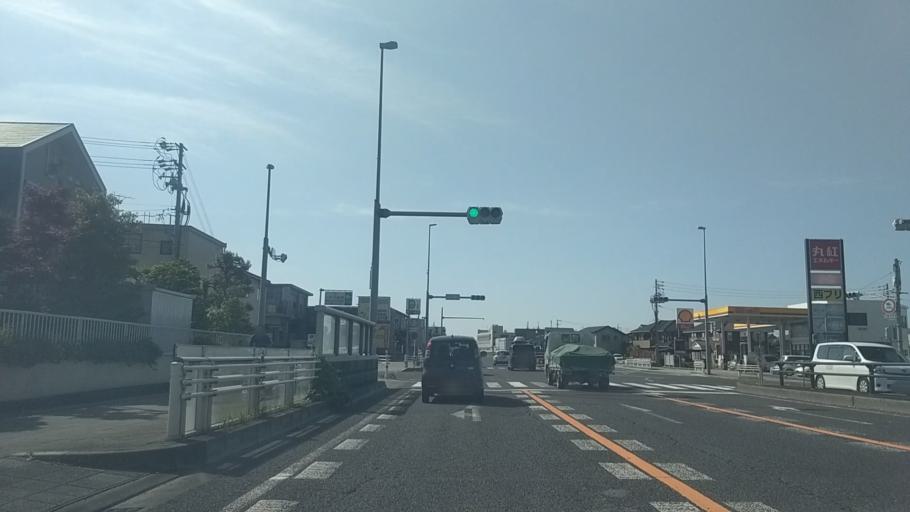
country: JP
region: Aichi
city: Anjo
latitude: 34.9901
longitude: 137.0826
